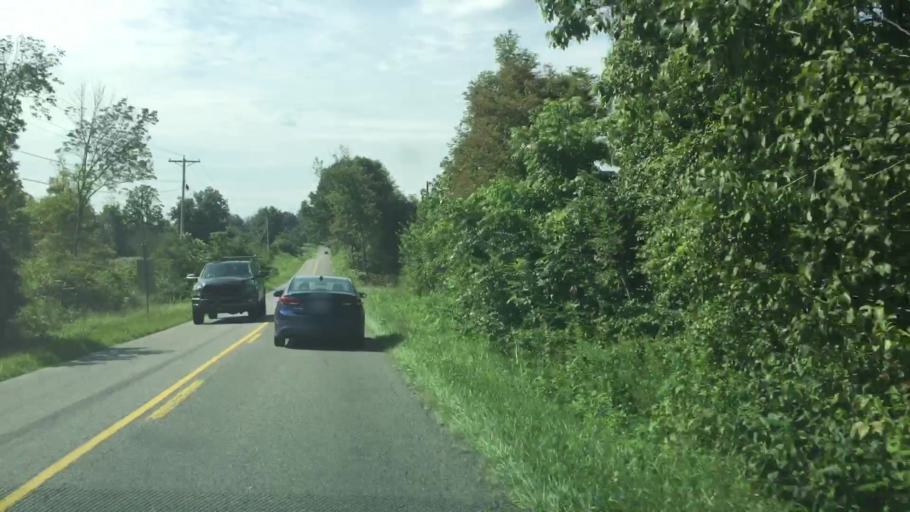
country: US
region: Tennessee
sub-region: Sullivan County
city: Fairmount
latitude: 36.6152
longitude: -82.0783
